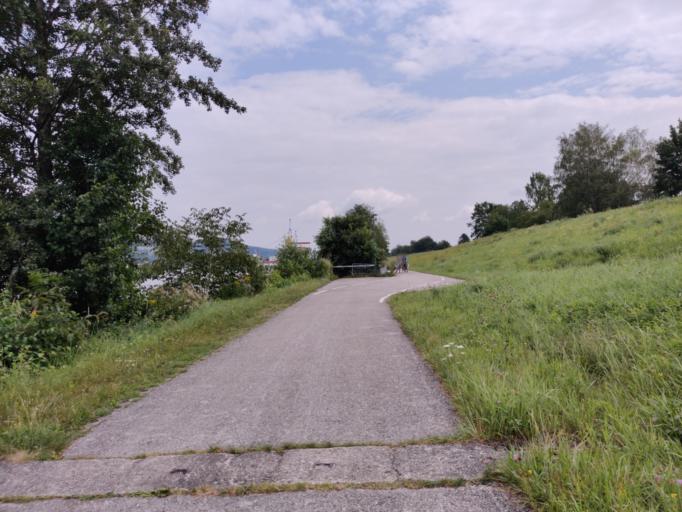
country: AT
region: Lower Austria
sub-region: Politischer Bezirk Melk
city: Marbach an der Donau
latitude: 48.2111
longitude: 15.1515
